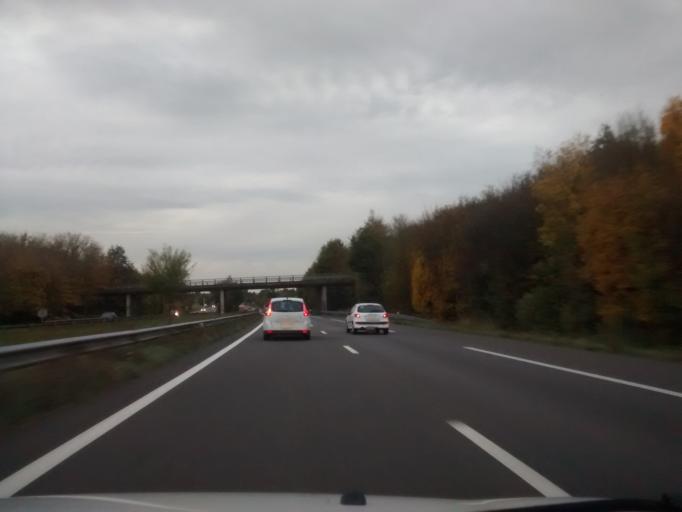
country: FR
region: Brittany
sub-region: Departement d'Ille-et-Vilaine
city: Montauban-de-Bretagne
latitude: 48.2074
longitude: -2.0441
